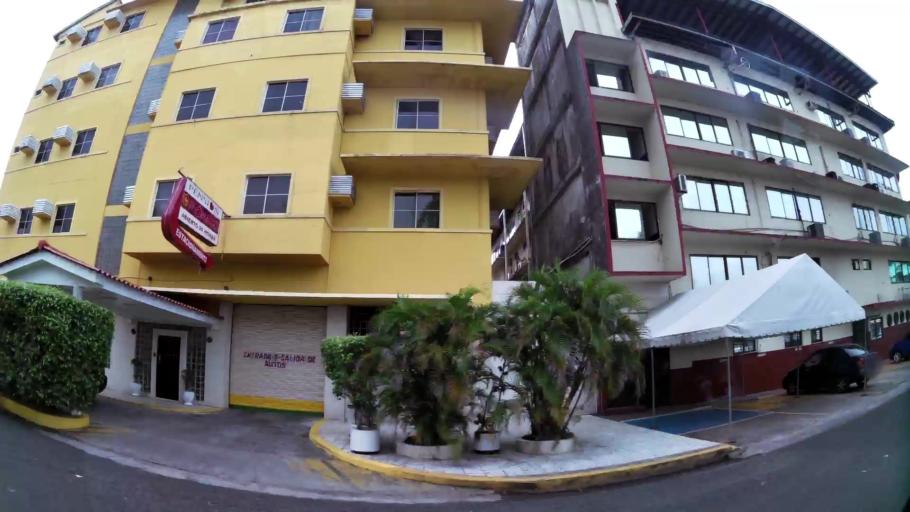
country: PA
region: Panama
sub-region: Distrito de Panama
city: Ancon
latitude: 8.9663
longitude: -79.5378
